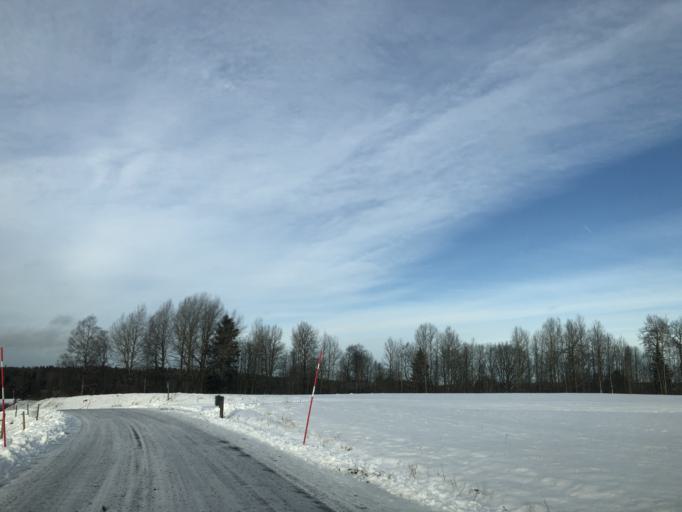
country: SE
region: Vaestra Goetaland
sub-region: Ulricehamns Kommun
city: Ulricehamn
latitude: 57.7866
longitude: 13.5271
